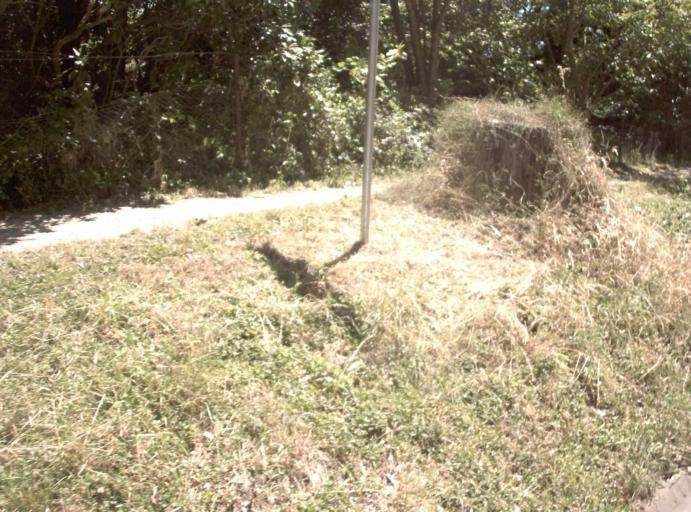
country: AU
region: Victoria
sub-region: Yarra Ranges
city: Ferny Creek
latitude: -37.8768
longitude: 145.3424
